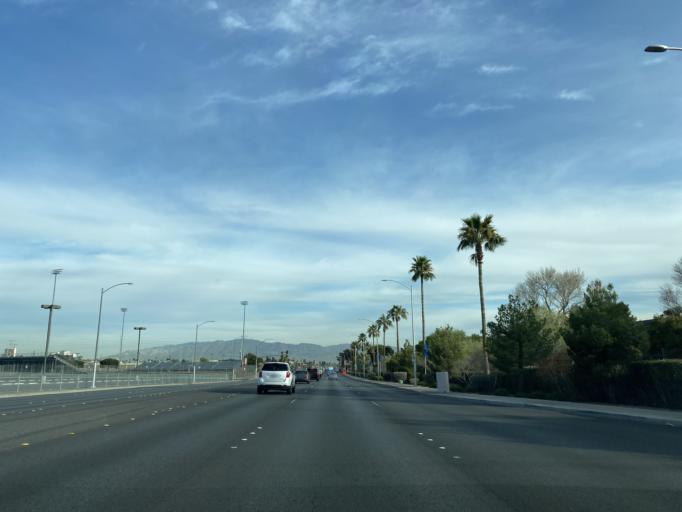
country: US
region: Nevada
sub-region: Clark County
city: Winchester
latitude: 36.1377
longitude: -115.1185
